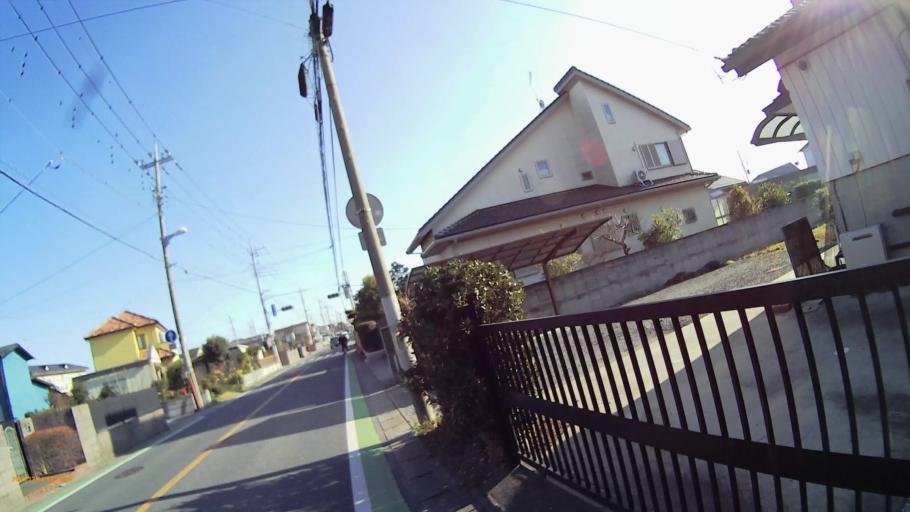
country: JP
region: Saitama
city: Fukiage-fujimi
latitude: 36.0797
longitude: 139.4790
